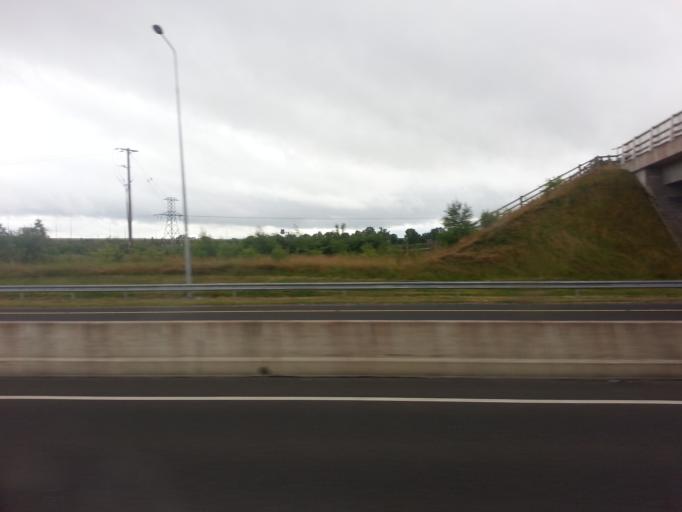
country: IE
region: Leinster
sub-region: Kilkenny
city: Kilkenny
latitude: 52.6348
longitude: -7.1509
